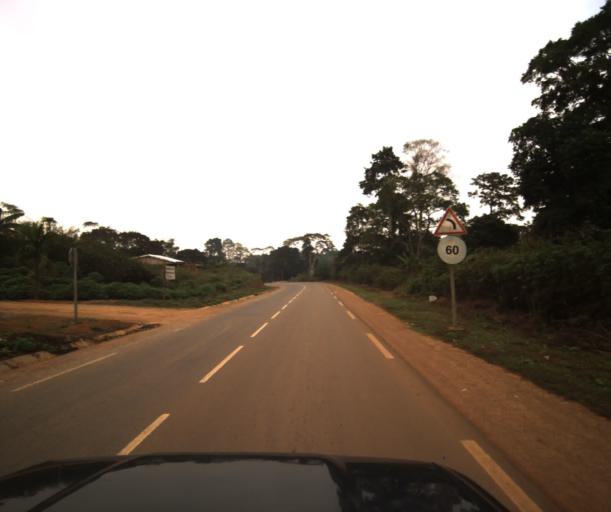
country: CM
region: Centre
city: Mbankomo
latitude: 3.7906
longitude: 11.4475
